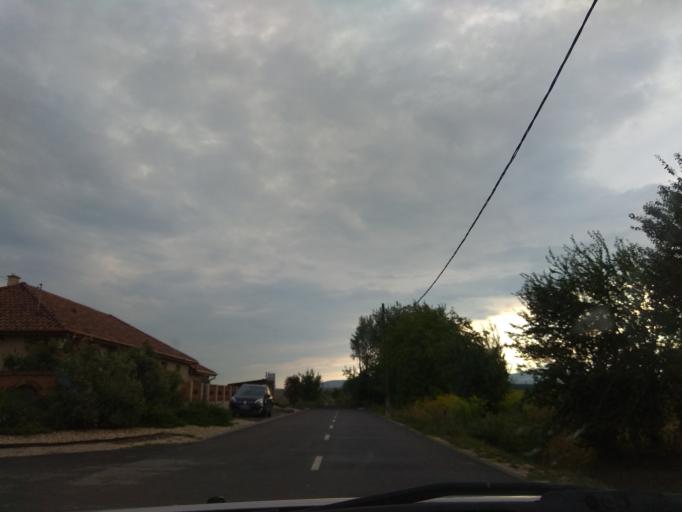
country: HU
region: Borsod-Abauj-Zemplen
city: Miskolc
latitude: 48.0757
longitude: 20.8187
